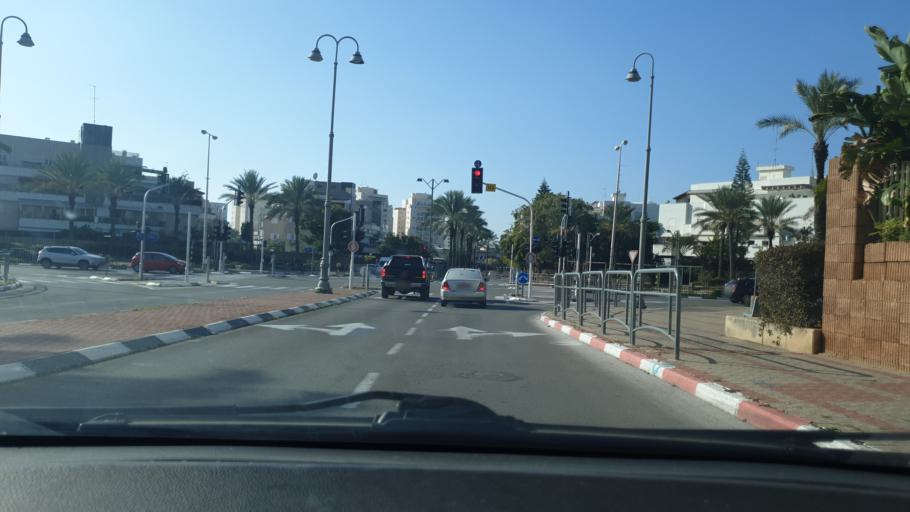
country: IL
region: Central District
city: Rishon LeZiyyon
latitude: 31.9743
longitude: 34.7770
